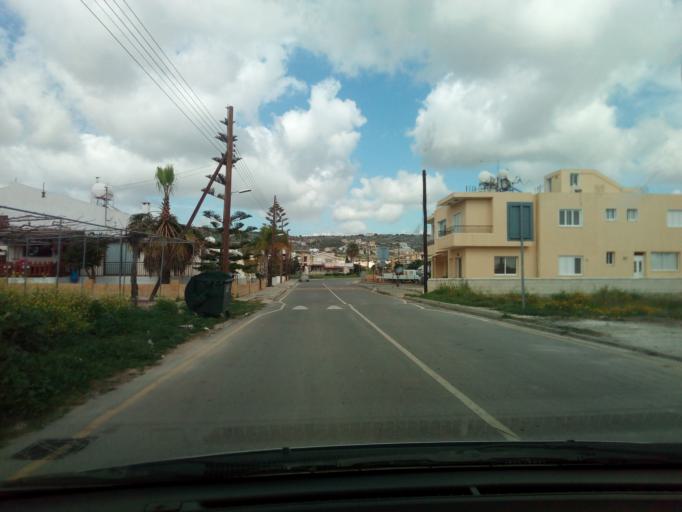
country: CY
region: Pafos
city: Paphos
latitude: 34.7610
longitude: 32.4559
